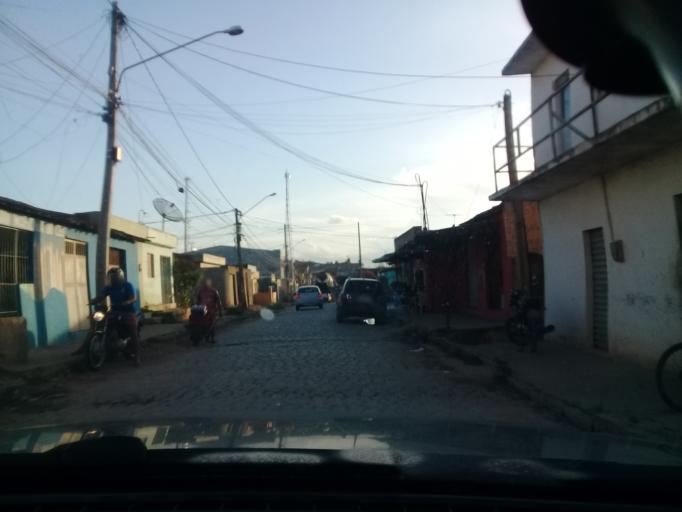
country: BR
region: Pernambuco
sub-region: Vitoria De Santo Antao
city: Vitoria de Santo Antao
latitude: -8.1278
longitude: -35.2848
